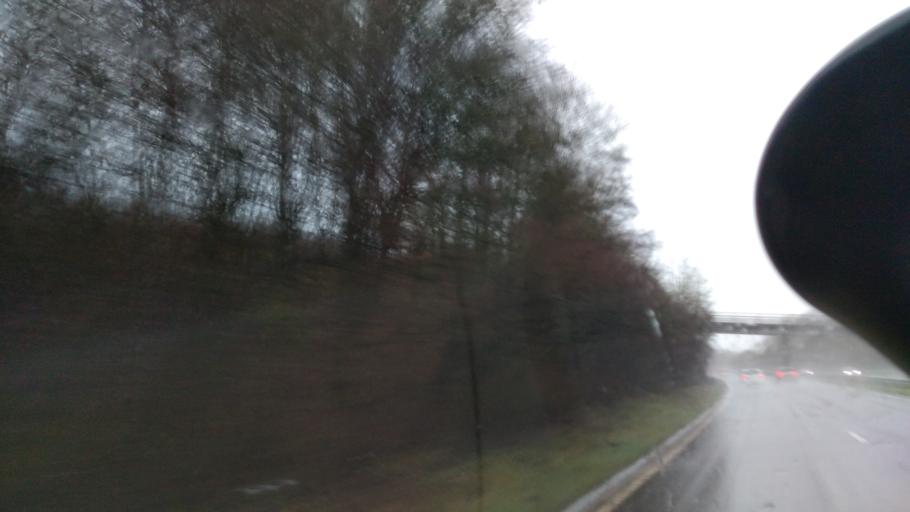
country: GB
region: England
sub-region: Brighton and Hove
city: Rottingdean
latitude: 50.8660
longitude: -0.0565
